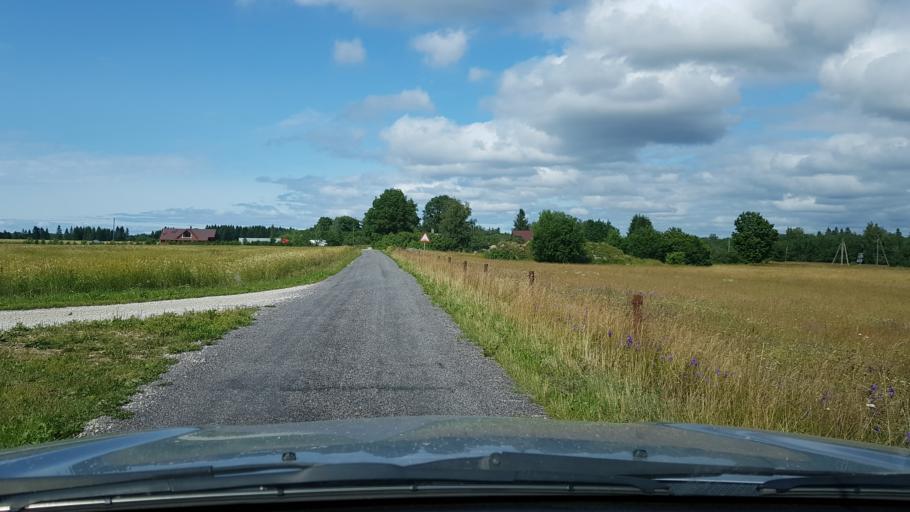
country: EE
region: Ida-Virumaa
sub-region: Narva-Joesuu linn
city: Narva-Joesuu
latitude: 59.3697
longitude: 27.9539
